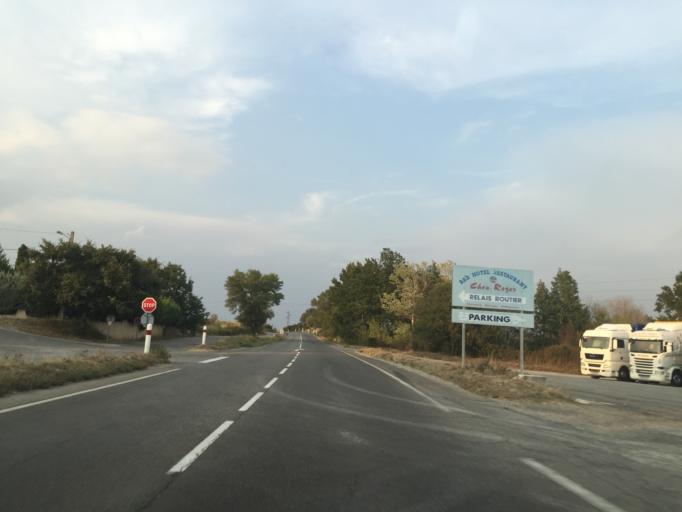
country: FR
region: Provence-Alpes-Cote d'Azur
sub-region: Departement des Alpes-de-Haute-Provence
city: Villeneuve
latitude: 43.8956
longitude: 5.8771
